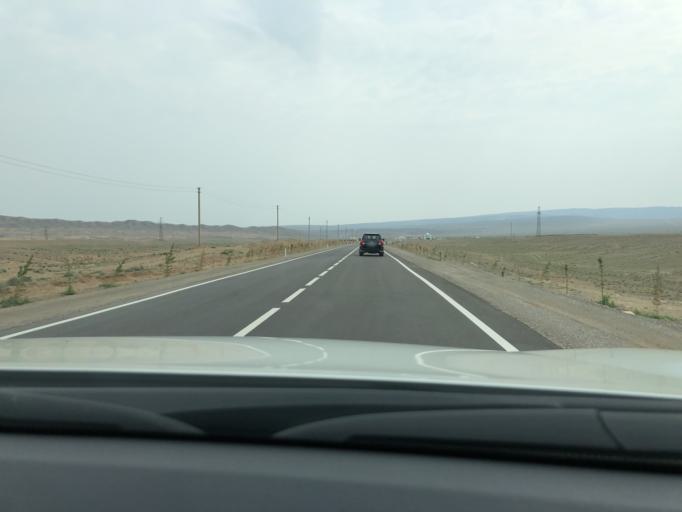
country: TJ
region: Viloyati Sughd
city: Kim
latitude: 40.1959
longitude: 70.4737
